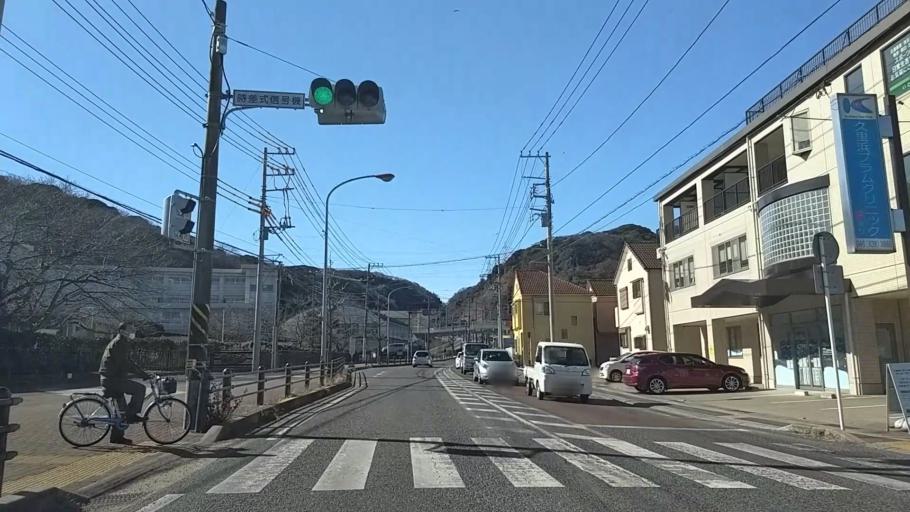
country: JP
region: Kanagawa
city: Yokosuka
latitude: 35.2268
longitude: 139.7011
